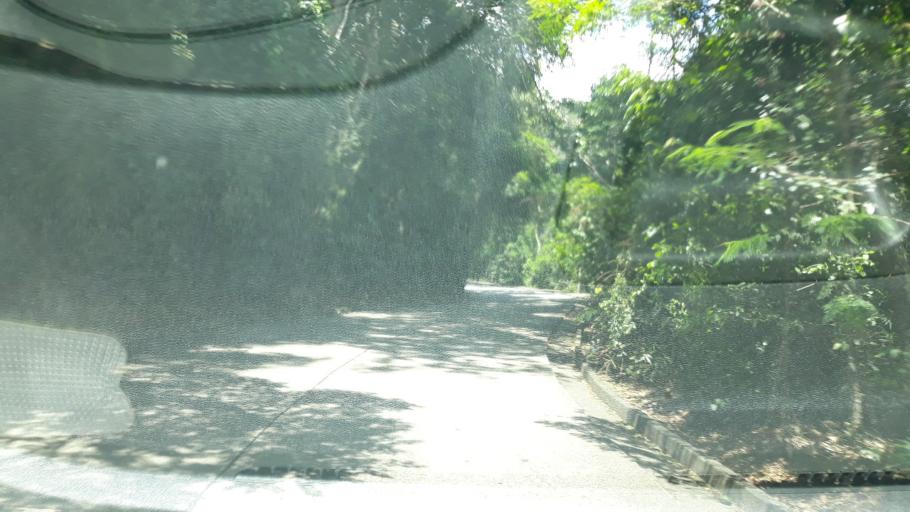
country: BR
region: Rio de Janeiro
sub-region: Rio De Janeiro
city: Rio de Janeiro
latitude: -22.9477
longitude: -43.2101
